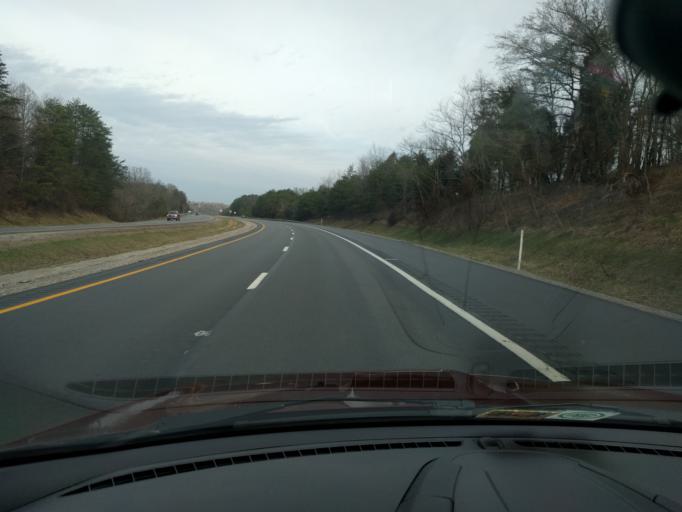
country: US
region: West Virginia
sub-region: Jackson County
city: Ripley
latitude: 38.7837
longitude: -81.7240
